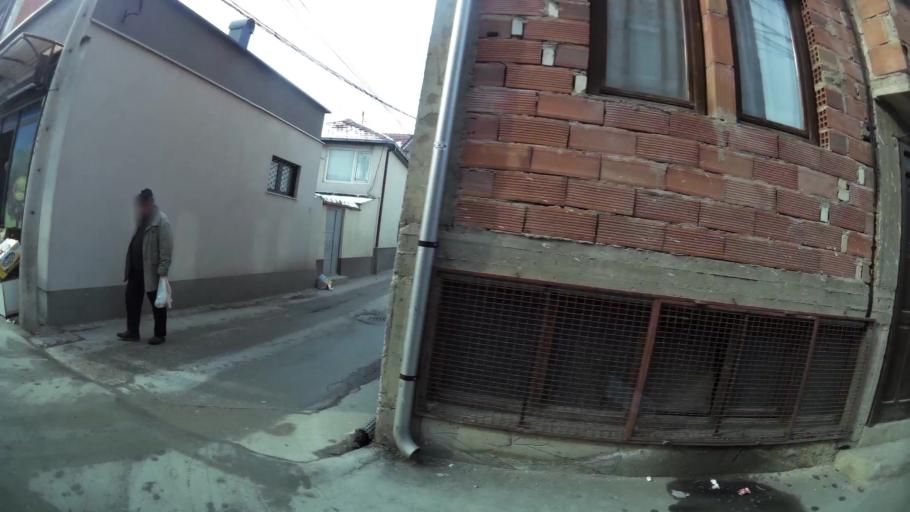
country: MK
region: Cair
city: Cair
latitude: 42.0087
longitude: 21.4372
